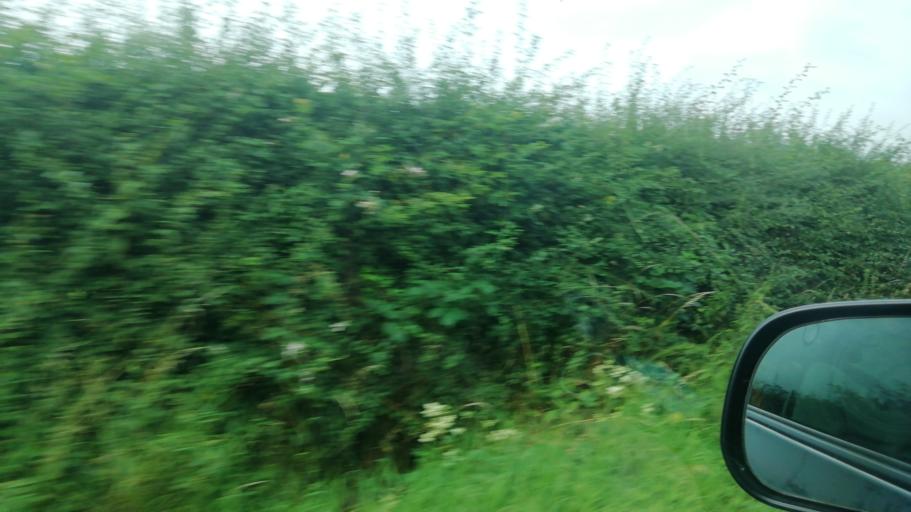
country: IE
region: Munster
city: Fethard
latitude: 52.5678
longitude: -7.5793
